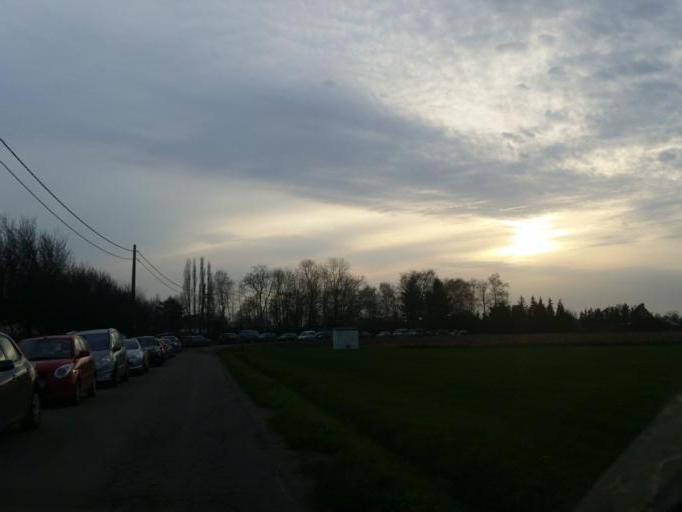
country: BE
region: Flanders
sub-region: Provincie Antwerpen
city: Lier
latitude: 51.1116
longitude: 4.5744
